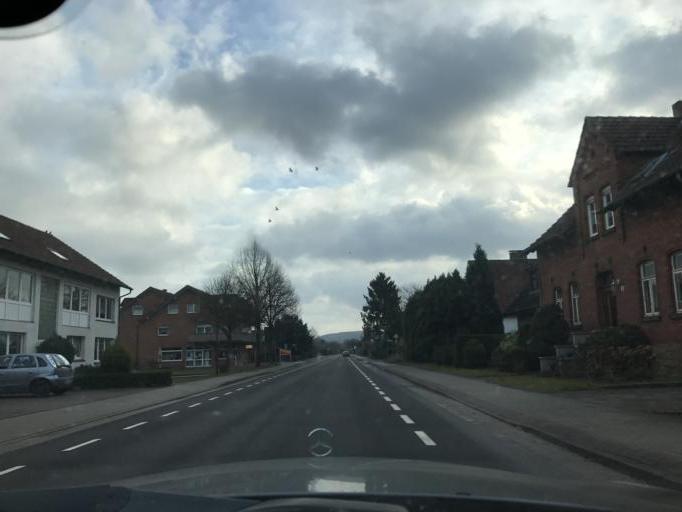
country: DE
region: Lower Saxony
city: Hasbergen
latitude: 52.2080
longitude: 7.9226
